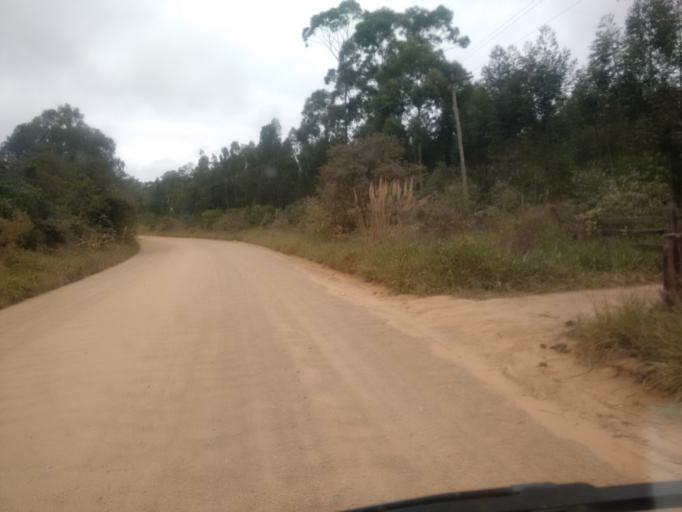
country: BR
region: Rio Grande do Sul
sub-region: Camaqua
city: Camaqua
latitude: -30.8023
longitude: -51.8298
